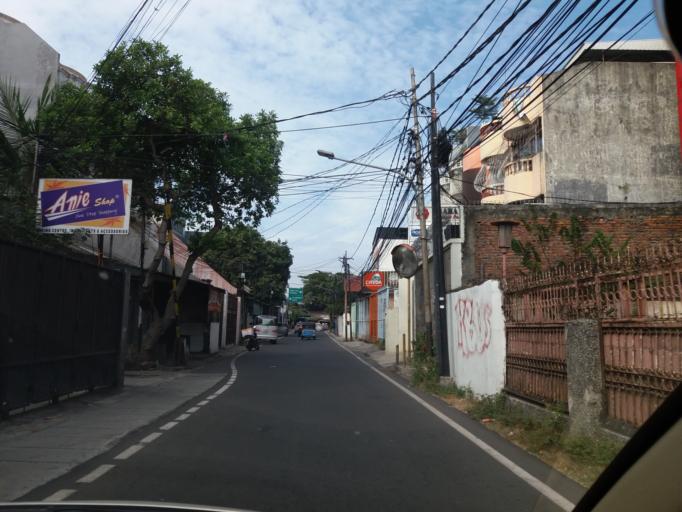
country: ID
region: Jakarta Raya
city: Jakarta
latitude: -6.1717
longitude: 106.8418
